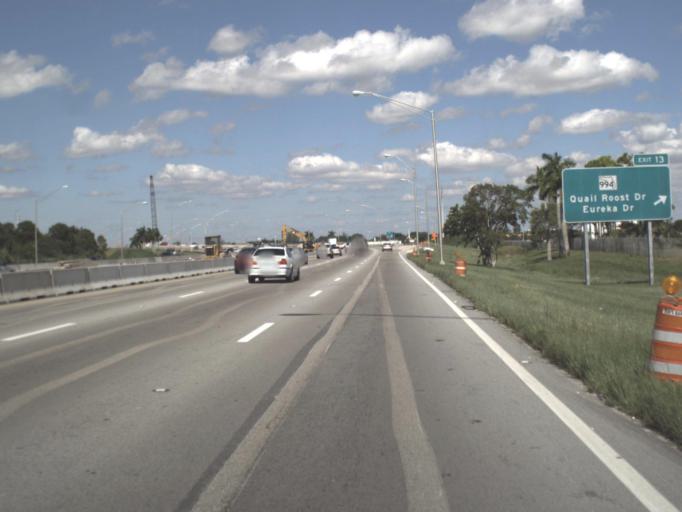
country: US
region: Florida
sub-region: Miami-Dade County
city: South Miami Heights
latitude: 25.5902
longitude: -80.3687
